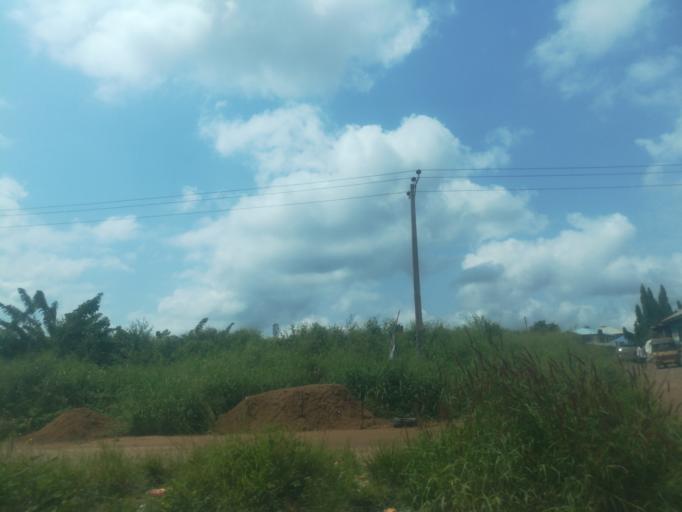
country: NG
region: Oyo
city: Ibadan
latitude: 7.3407
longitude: 3.8522
